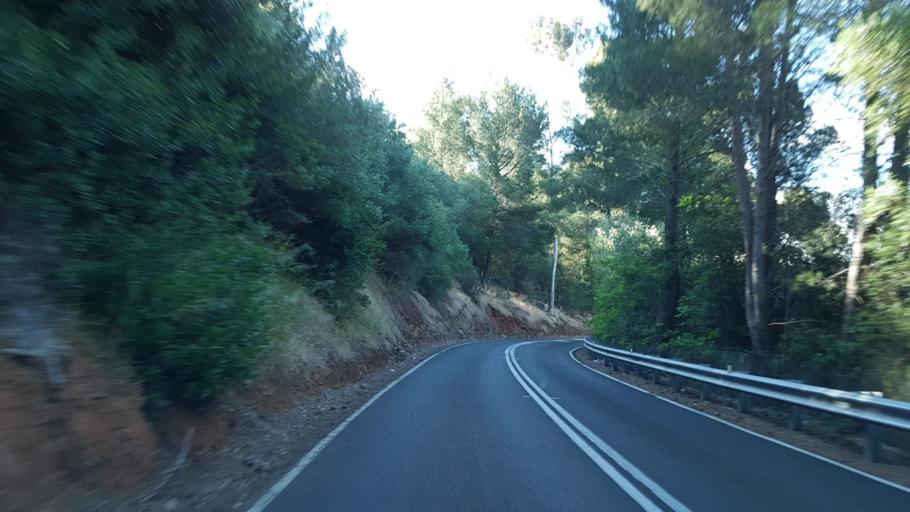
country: AU
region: South Australia
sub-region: Adelaide Hills
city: Adelaide Hills
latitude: -34.9116
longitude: 138.6945
